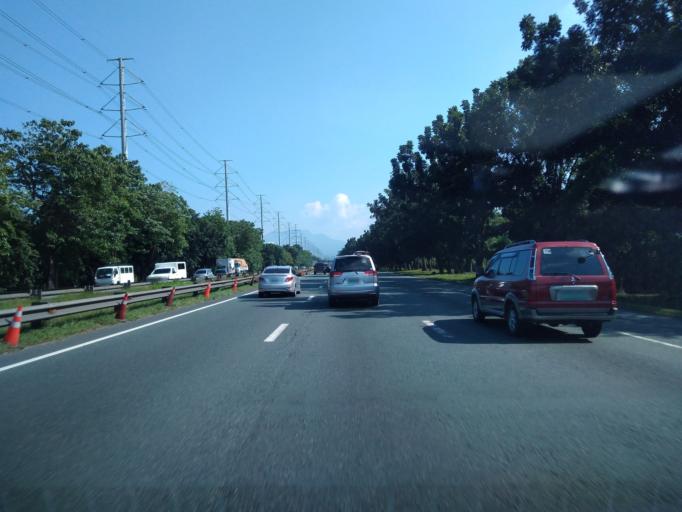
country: PH
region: Calabarzon
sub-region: Province of Laguna
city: Cabuyao
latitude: 14.2485
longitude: 121.1071
